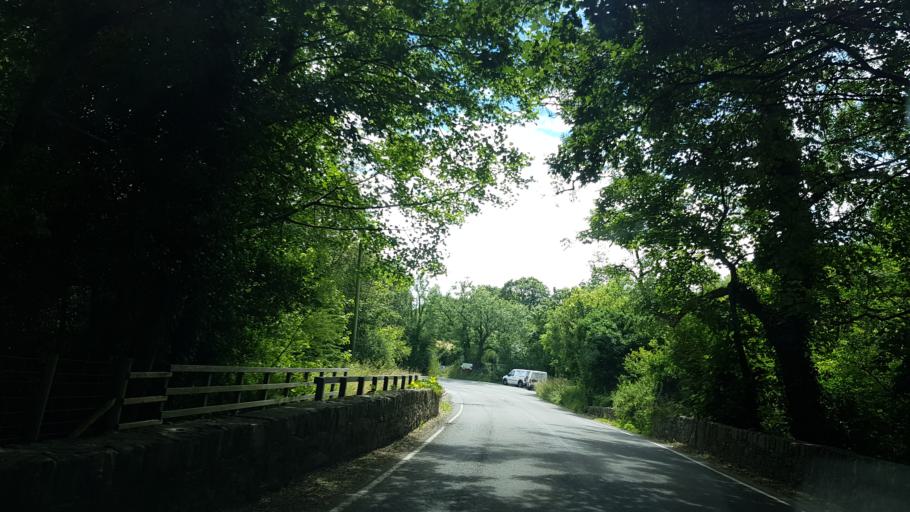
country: GB
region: Wales
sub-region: Pembrokeshire
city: Haverfordwest
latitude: 51.8202
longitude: -4.9535
